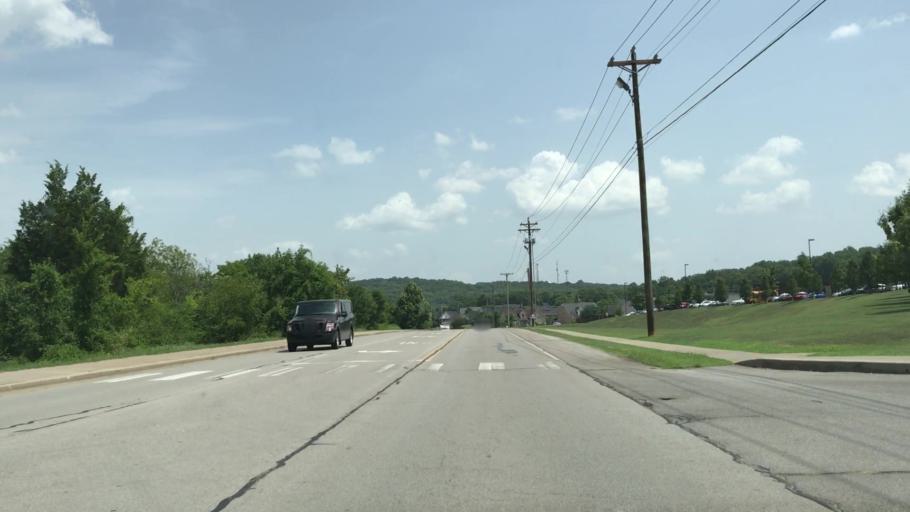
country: US
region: Tennessee
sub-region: Rutherford County
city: La Vergne
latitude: 35.9616
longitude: -86.5746
